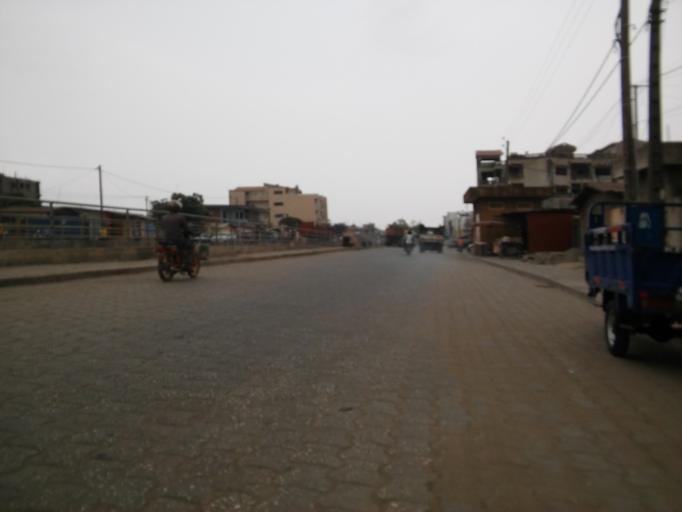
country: BJ
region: Littoral
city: Cotonou
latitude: 6.3784
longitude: 2.3981
